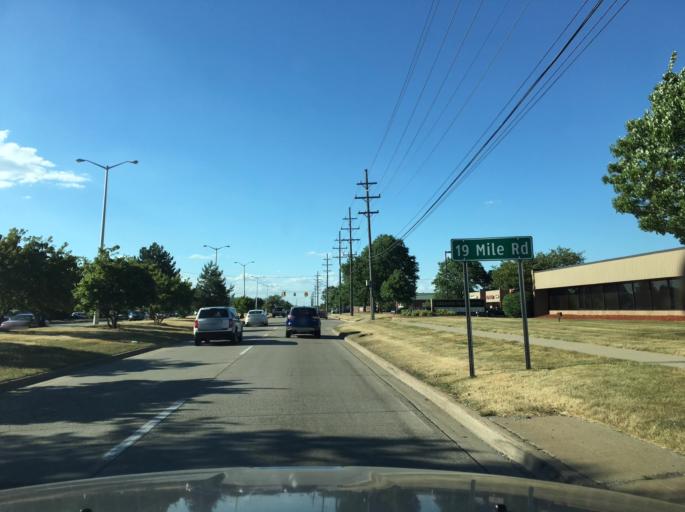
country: US
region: Michigan
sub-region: Macomb County
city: Utica
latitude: 42.6089
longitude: -82.9919
